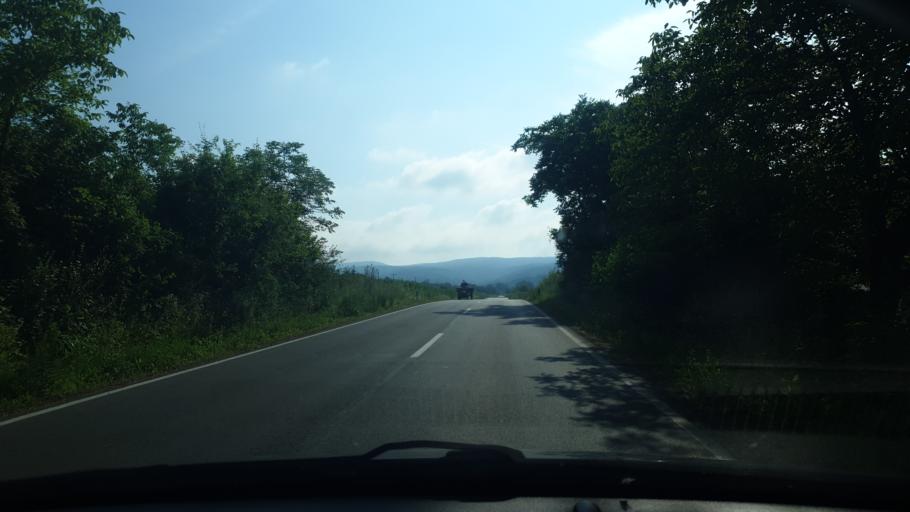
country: RS
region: Central Serbia
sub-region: Pomoravski Okrug
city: Cuprija
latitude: 43.9552
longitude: 21.4577
